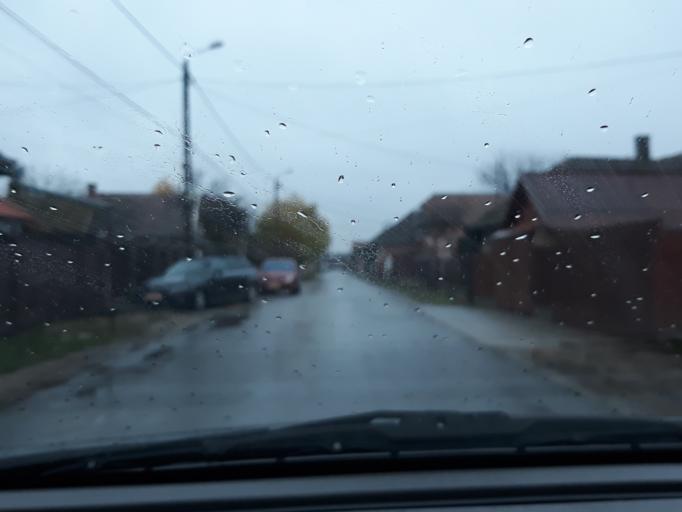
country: RO
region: Bihor
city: Margita
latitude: 47.3500
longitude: 22.3512
